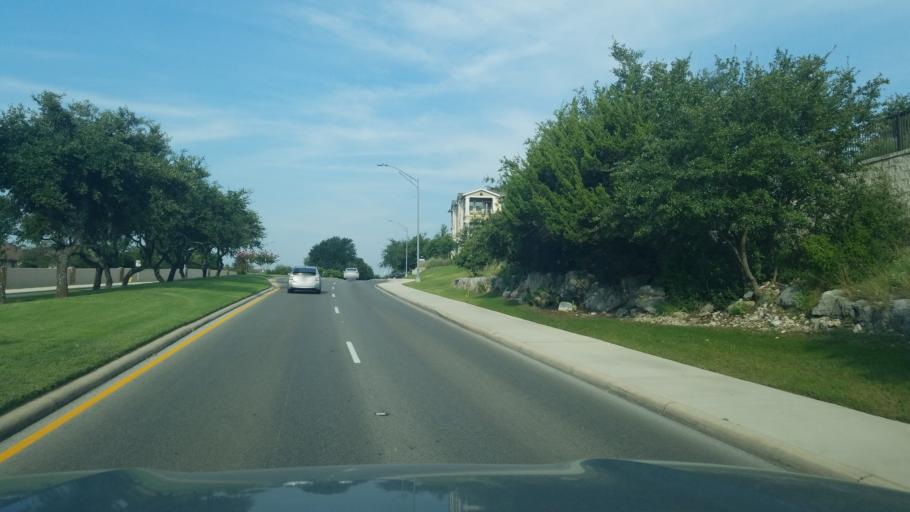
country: US
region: Texas
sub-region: Bexar County
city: Hollywood Park
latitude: 29.6452
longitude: -98.4705
